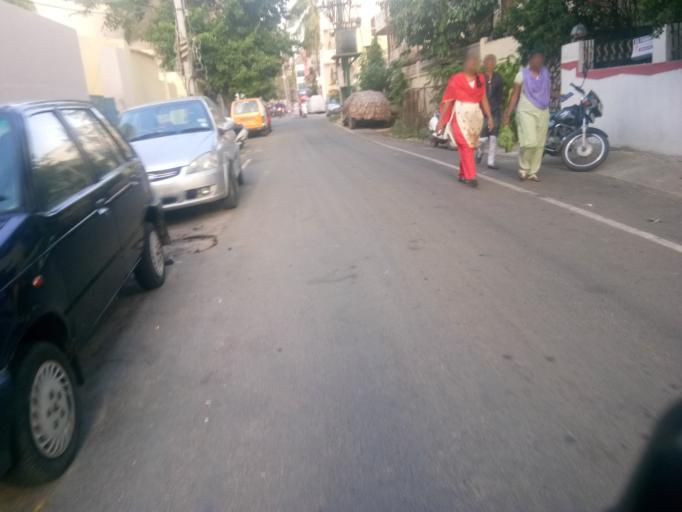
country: IN
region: Karnataka
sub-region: Bangalore Urban
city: Bangalore
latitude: 13.0123
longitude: 77.6247
